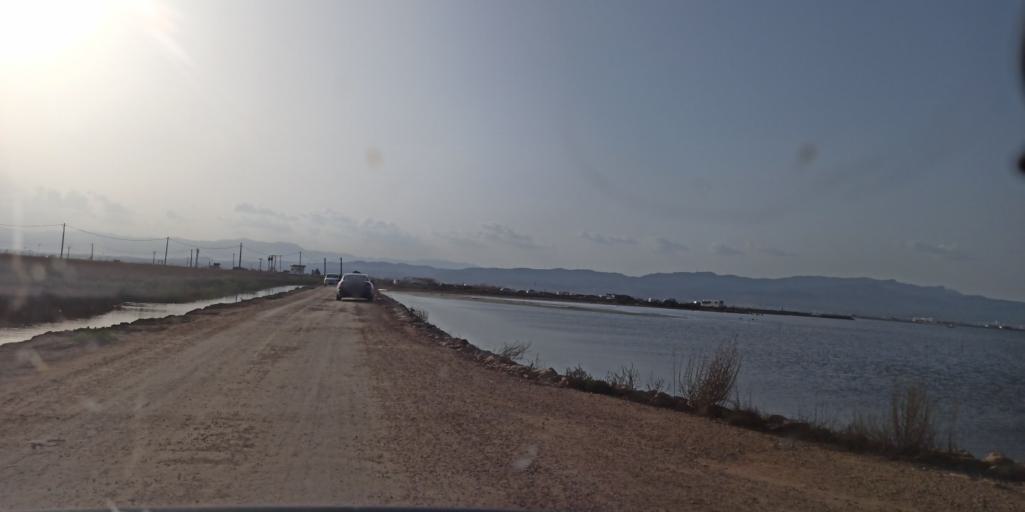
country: ES
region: Catalonia
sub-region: Provincia de Tarragona
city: L'Ampolla
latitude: 40.7657
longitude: 0.7424
